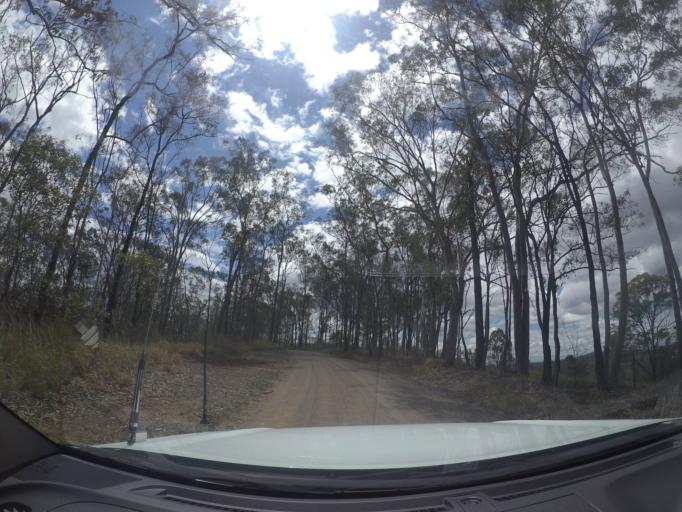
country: AU
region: Queensland
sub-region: Logan
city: Cedar Vale
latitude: -27.8928
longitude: 153.0456
